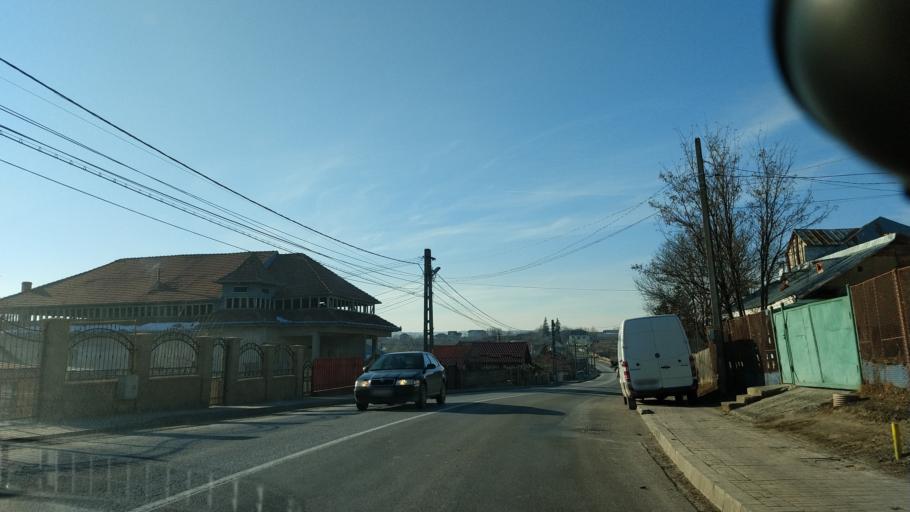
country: RO
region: Iasi
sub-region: Comuna Targu Frumos
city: Targu Frumos
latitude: 47.2030
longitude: 27.0053
